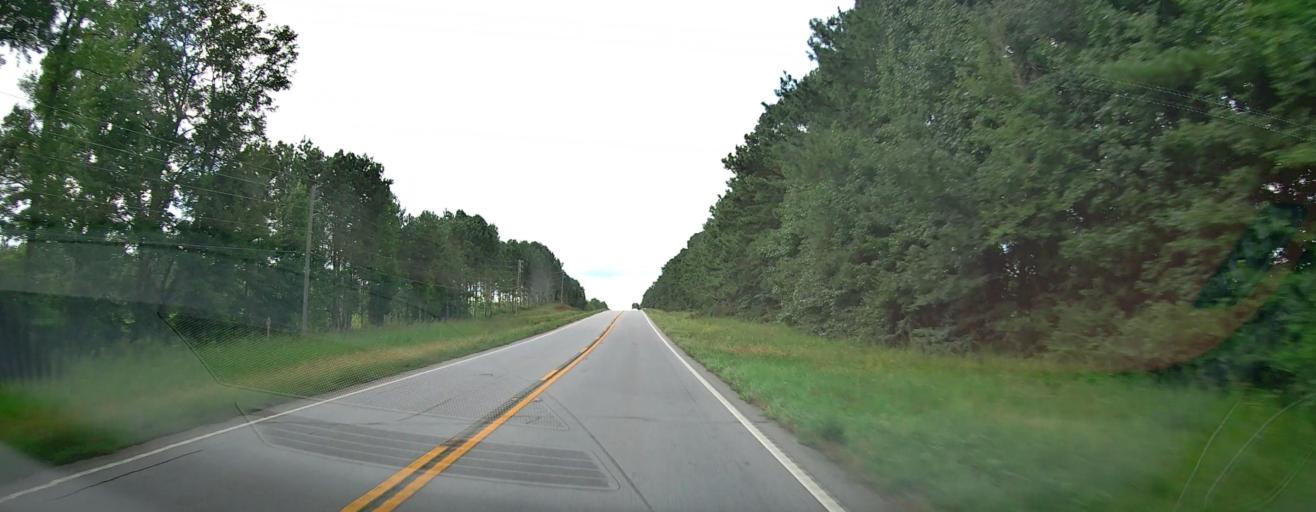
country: US
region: Georgia
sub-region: Meriwether County
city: Greenville
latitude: 33.0588
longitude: -84.5700
